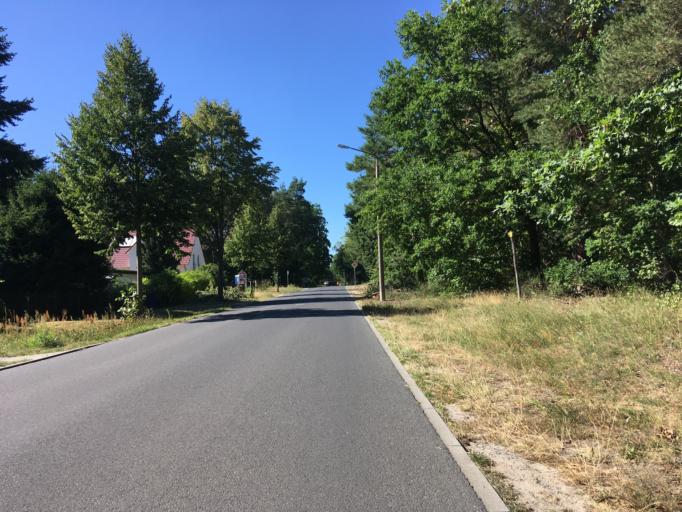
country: DE
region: Brandenburg
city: Schulzendorf
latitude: 52.3503
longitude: 13.5967
